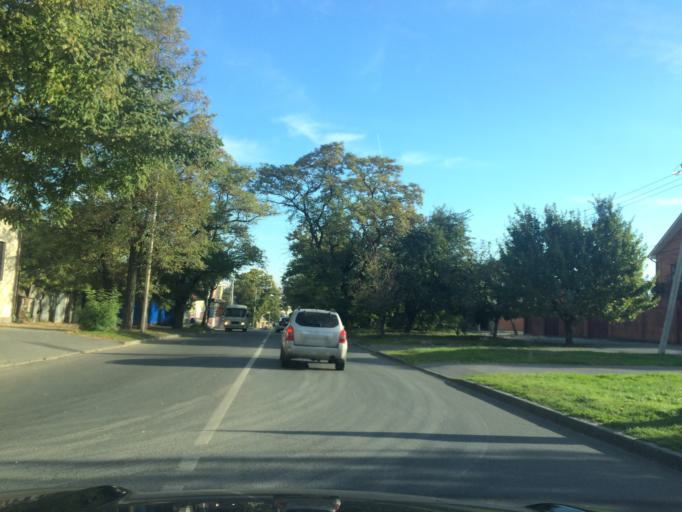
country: RU
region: Rostov
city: Rostov-na-Donu
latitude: 47.2094
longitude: 39.6913
